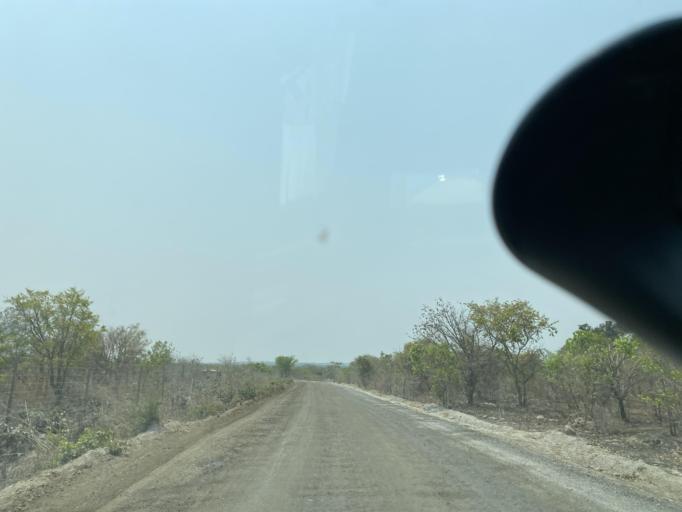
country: ZM
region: Lusaka
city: Lusaka
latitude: -15.5382
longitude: 28.4484
